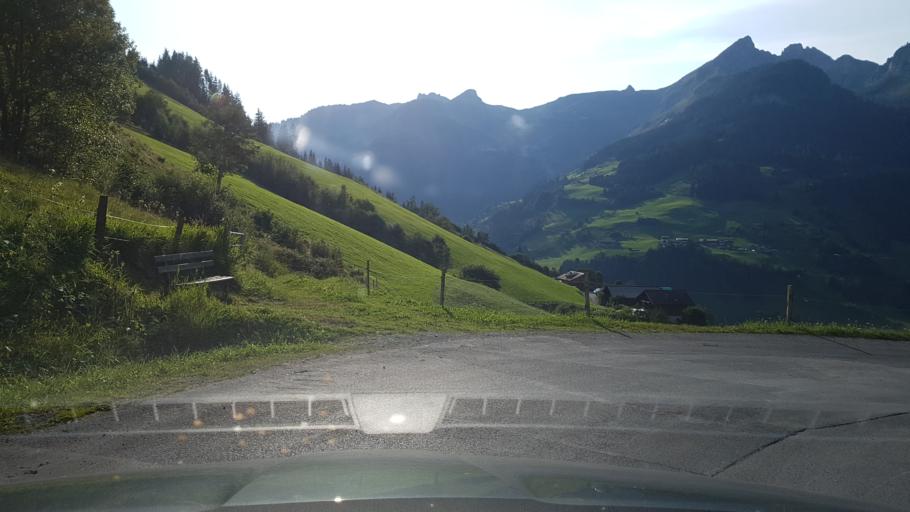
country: AT
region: Salzburg
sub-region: Politischer Bezirk Sankt Johann im Pongau
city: Sankt Johann im Pongau
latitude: 47.2757
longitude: 13.2280
